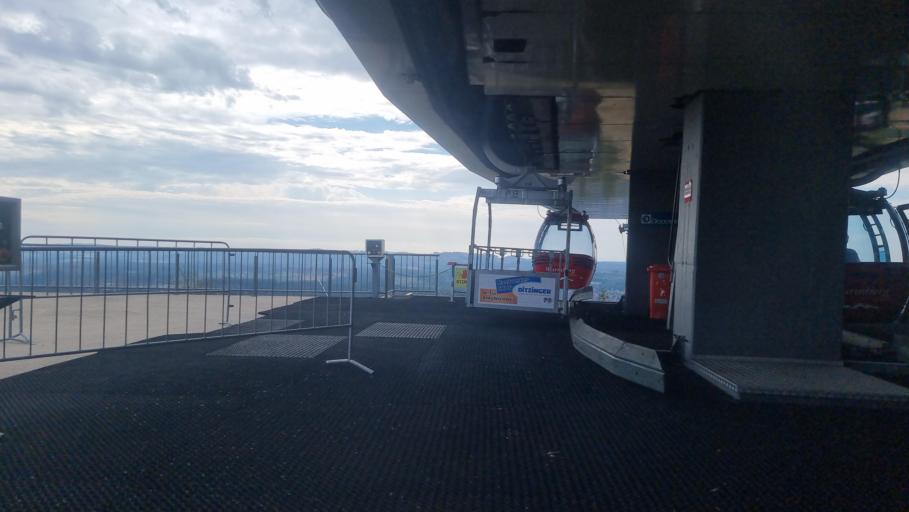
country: DE
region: Lower Saxony
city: Braunlage
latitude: 51.7445
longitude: 10.6174
